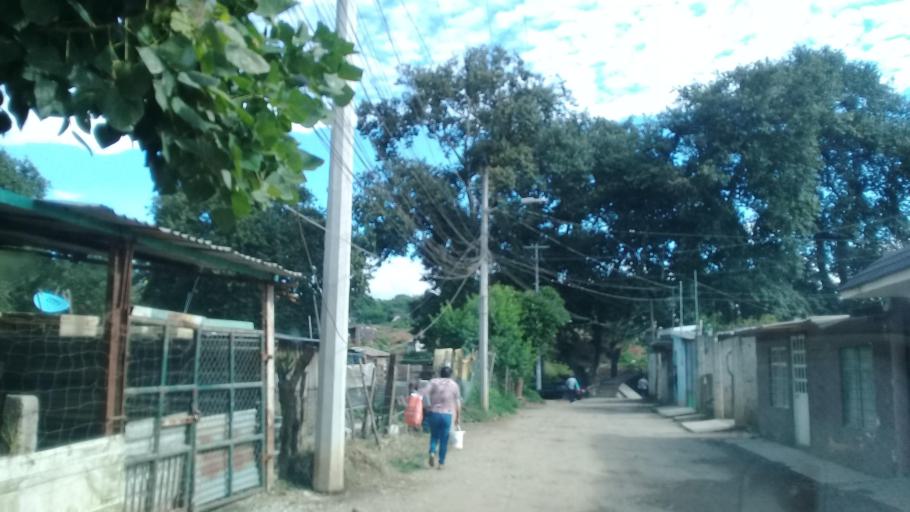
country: MX
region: Veracruz
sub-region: Jilotepec
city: El Pueblito (Garbanzal)
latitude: 19.5758
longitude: -96.9102
